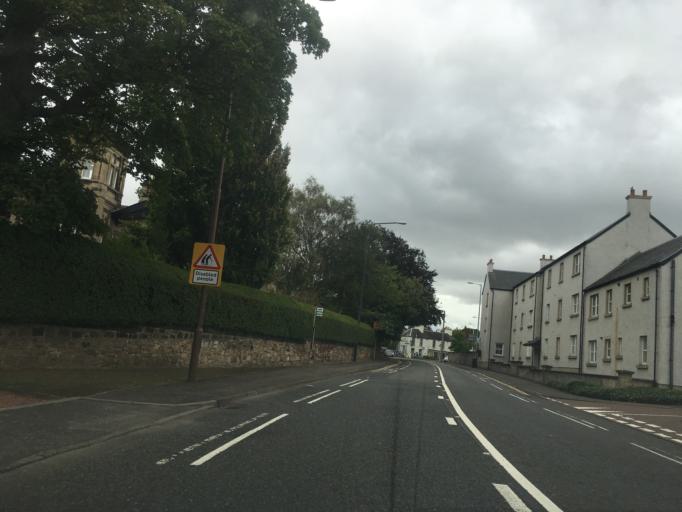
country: GB
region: Scotland
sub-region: Midlothian
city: Dalkeith
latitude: 55.8895
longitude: -3.0822
